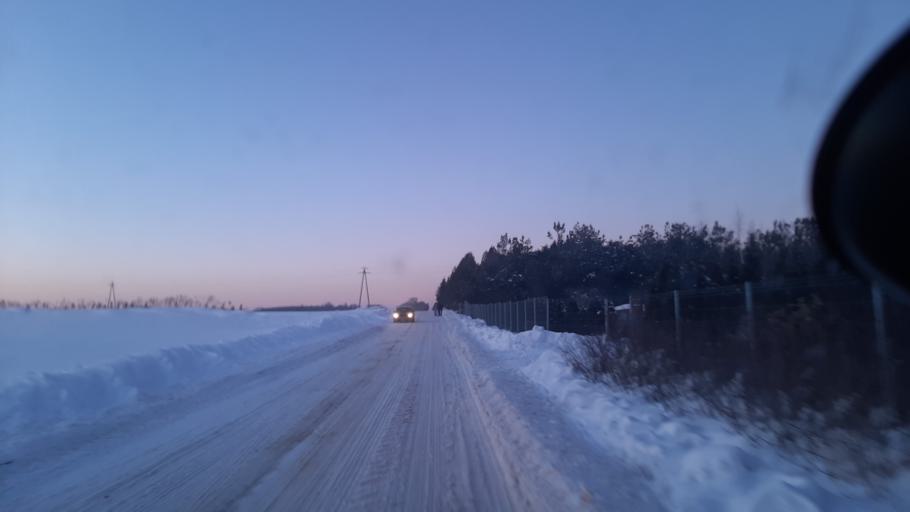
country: PL
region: Lublin Voivodeship
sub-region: Powiat lubelski
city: Jastkow
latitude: 51.3644
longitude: 22.5281
